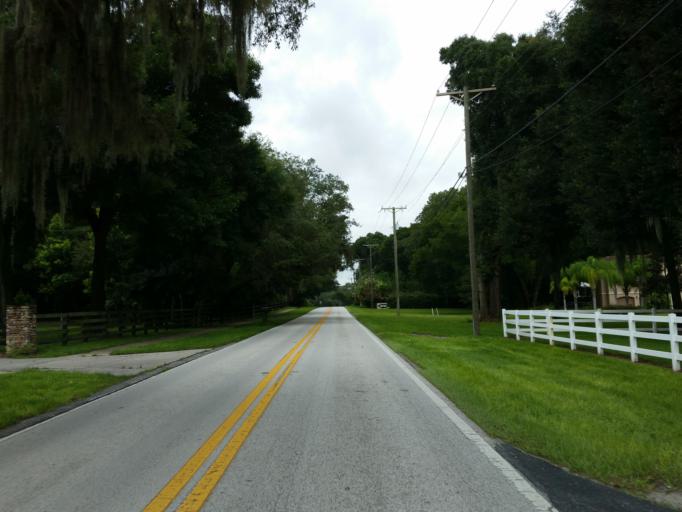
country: US
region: Florida
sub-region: Hillsborough County
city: Thonotosassa
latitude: 28.0526
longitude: -82.2867
